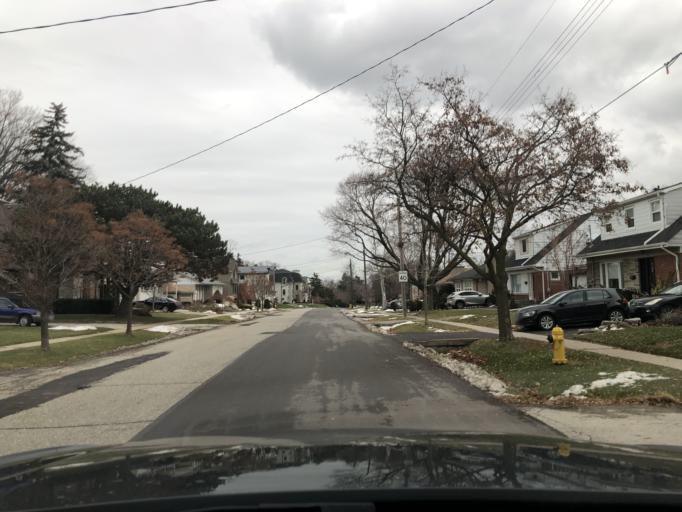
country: CA
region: Ontario
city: Etobicoke
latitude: 43.6999
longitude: -79.5384
